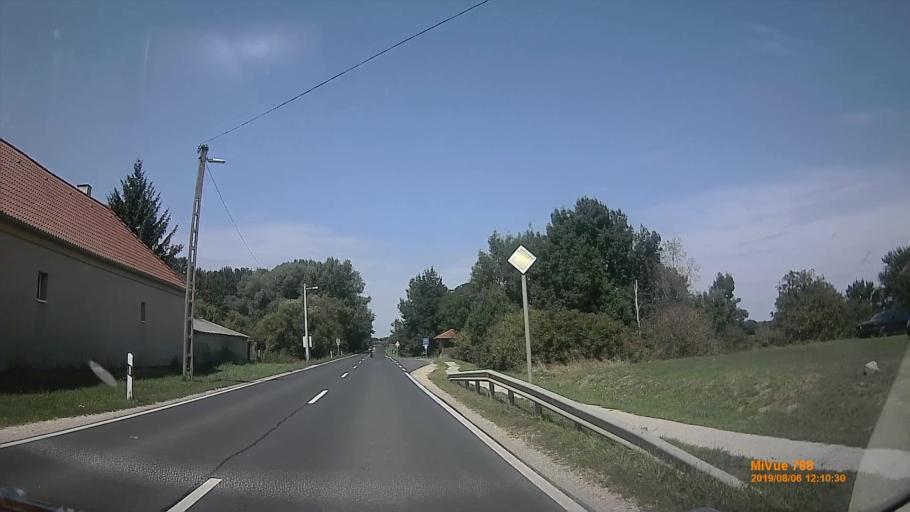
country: HU
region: Vas
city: Vasvar
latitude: 47.1037
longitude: 16.8712
